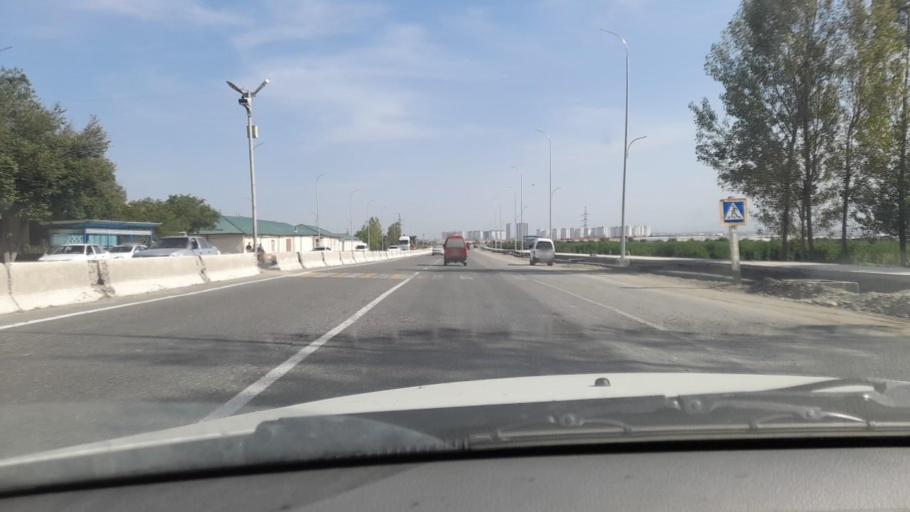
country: UZ
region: Samarqand
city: Daxbet
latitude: 39.7451
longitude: 66.9242
